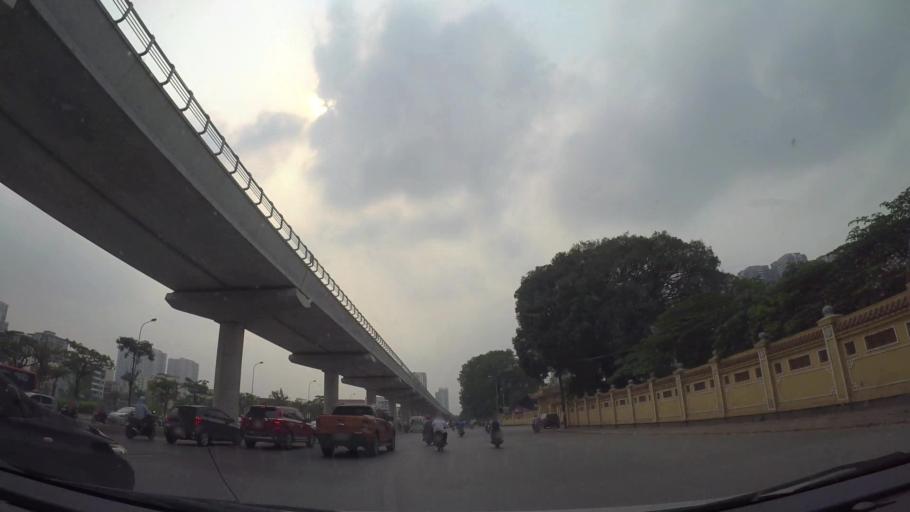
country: VN
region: Ha Noi
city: Cau Dien
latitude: 21.0393
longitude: 105.7699
